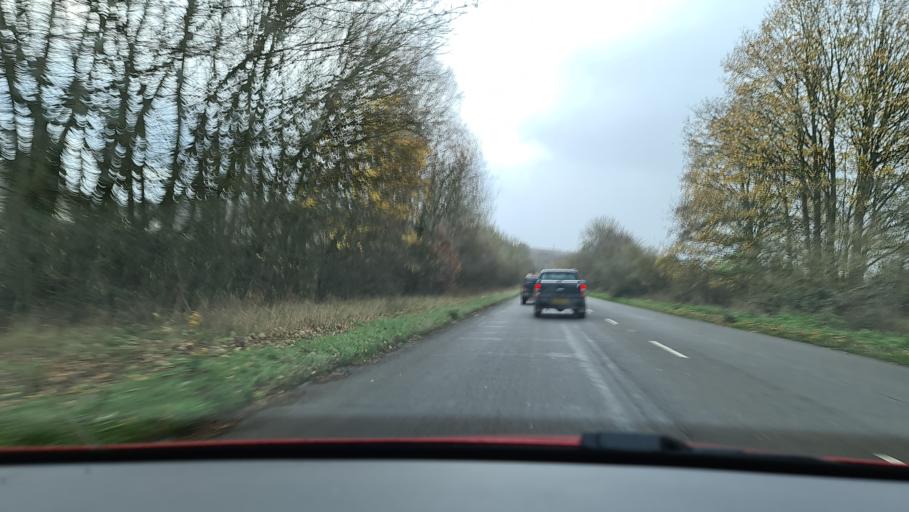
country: GB
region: England
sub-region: Buckinghamshire
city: Great Missenden
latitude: 51.7093
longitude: -0.7091
